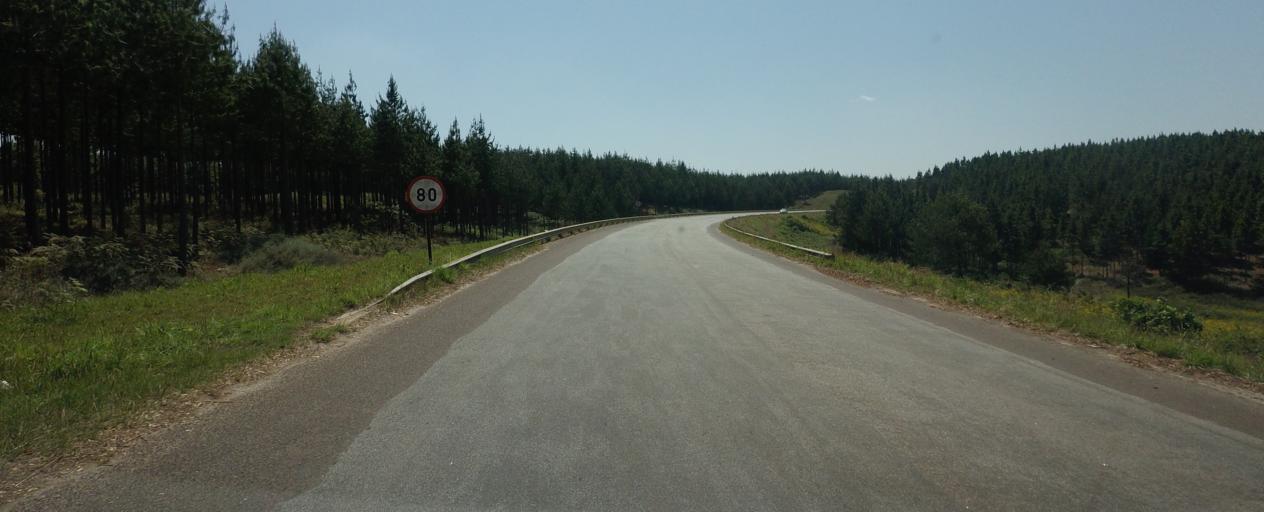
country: ZA
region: Mpumalanga
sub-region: Ehlanzeni District
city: Graksop
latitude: -24.9124
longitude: 30.8421
